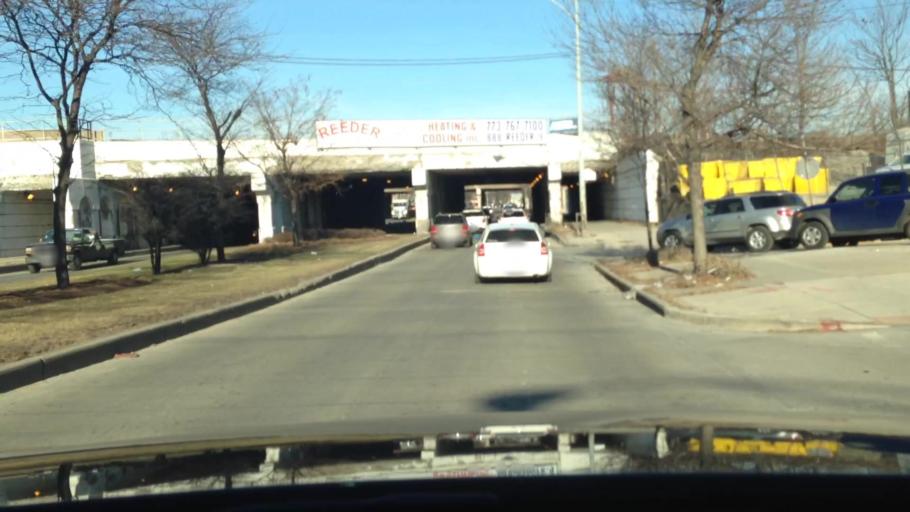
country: US
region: Illinois
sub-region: Cook County
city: Chicago
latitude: 41.8880
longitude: -87.6612
